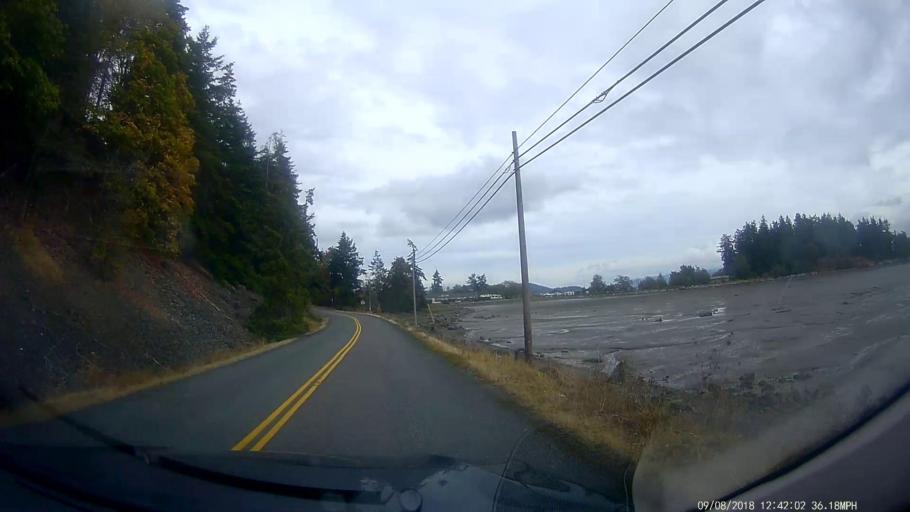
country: US
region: Washington
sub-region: Skagit County
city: Anacortes
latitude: 48.4804
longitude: -122.5928
